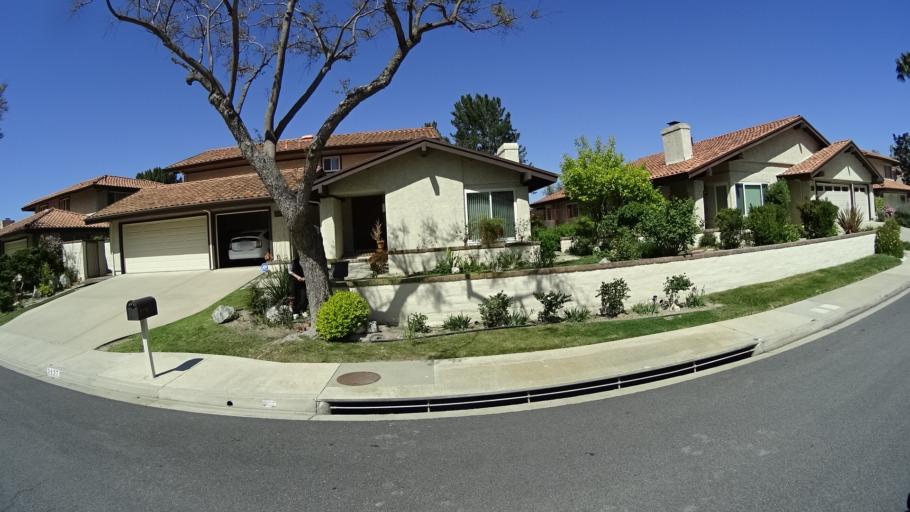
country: US
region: California
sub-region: Ventura County
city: Moorpark
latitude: 34.2333
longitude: -118.8508
